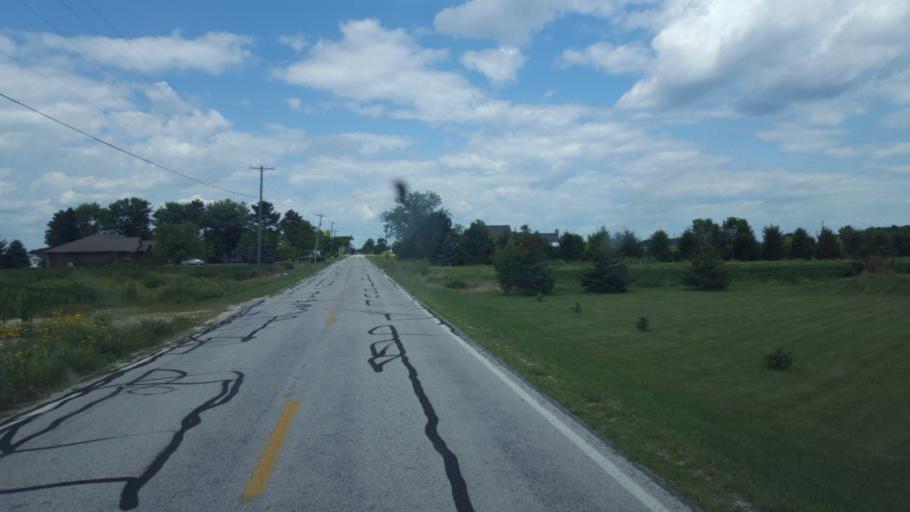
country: US
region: Ohio
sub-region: Lucas County
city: Curtice
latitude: 41.5926
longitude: -83.2804
